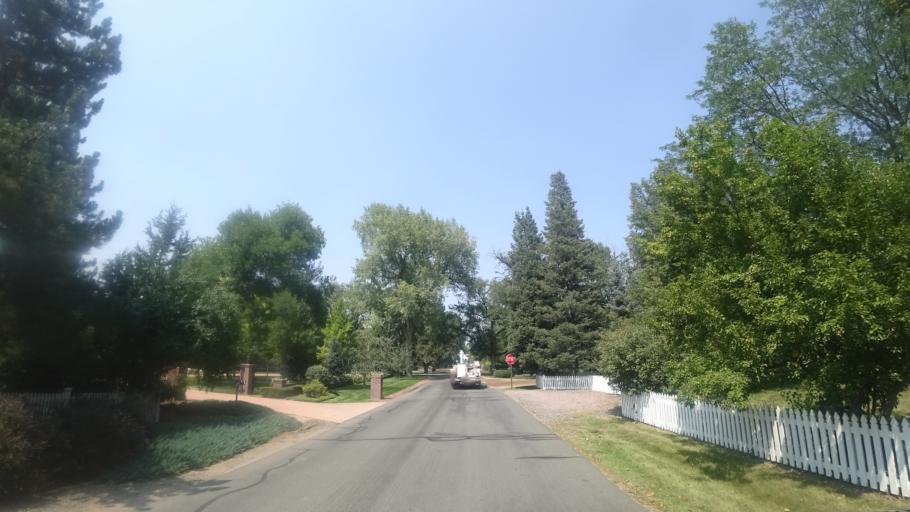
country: US
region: Colorado
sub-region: Arapahoe County
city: Cherry Hills Village
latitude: 39.6259
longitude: -104.9691
